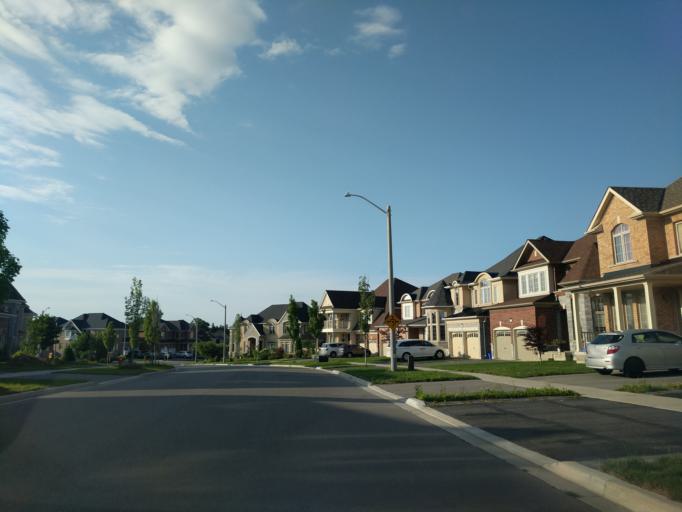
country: CA
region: Ontario
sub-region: York
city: Richmond Hill
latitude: 43.9013
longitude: -79.4520
